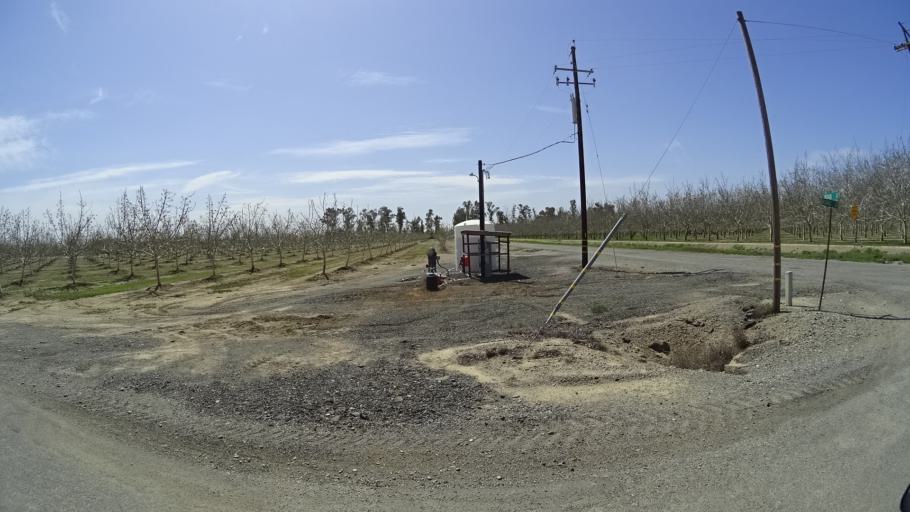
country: US
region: California
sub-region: Glenn County
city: Hamilton City
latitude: 39.6379
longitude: -122.0741
